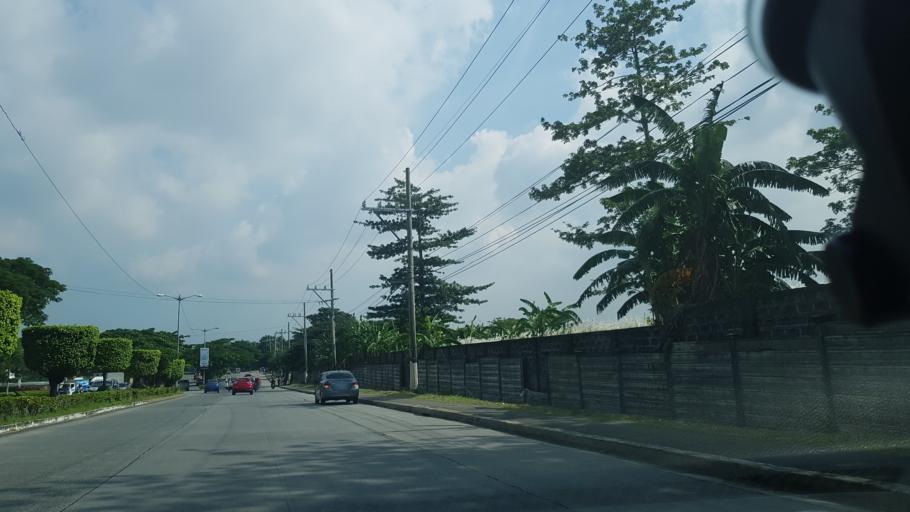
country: PH
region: Calabarzon
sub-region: Province of Laguna
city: San Pedro
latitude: 14.3775
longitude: 121.0132
